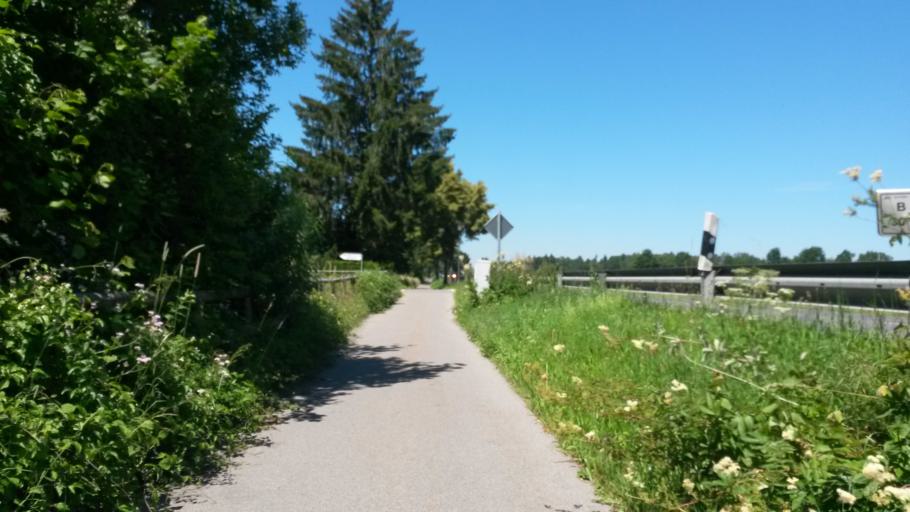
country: DE
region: Bavaria
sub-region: Upper Bavaria
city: Grassau
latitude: 47.7806
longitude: 12.4374
